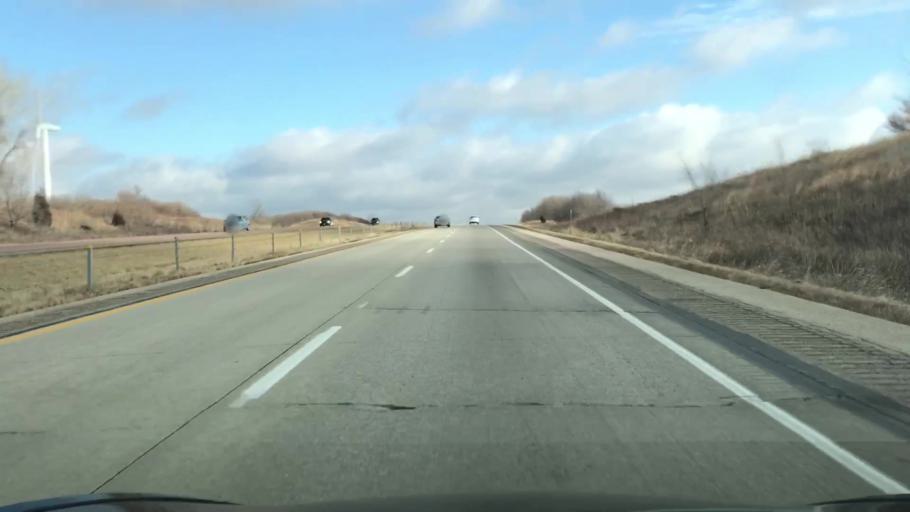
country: US
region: Iowa
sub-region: Guthrie County
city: Guthrie Center
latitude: 41.4969
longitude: -94.6955
